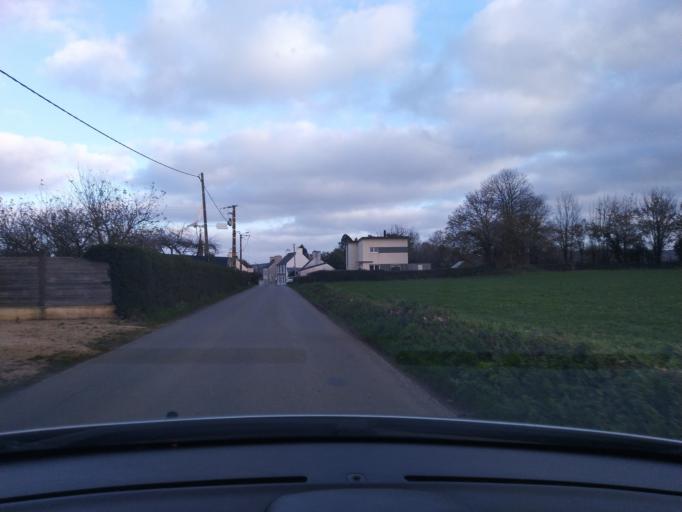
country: FR
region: Brittany
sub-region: Departement du Finistere
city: Plouigneau
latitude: 48.5657
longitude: -3.6503
